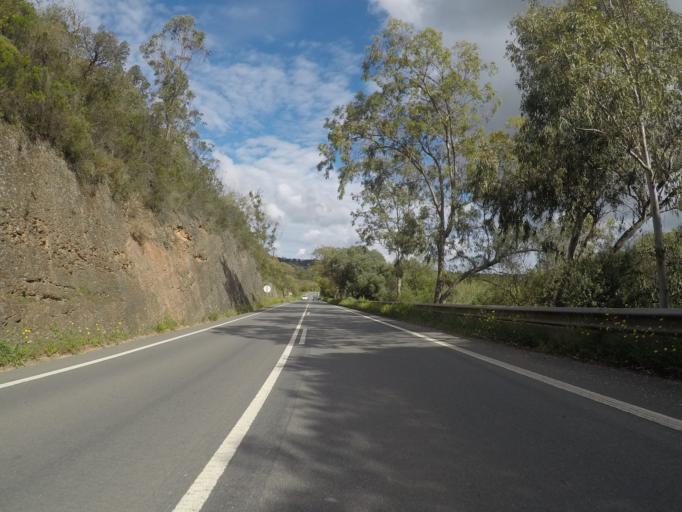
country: PT
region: Faro
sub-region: Aljezur
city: Aljezur
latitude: 37.2960
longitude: -8.7976
